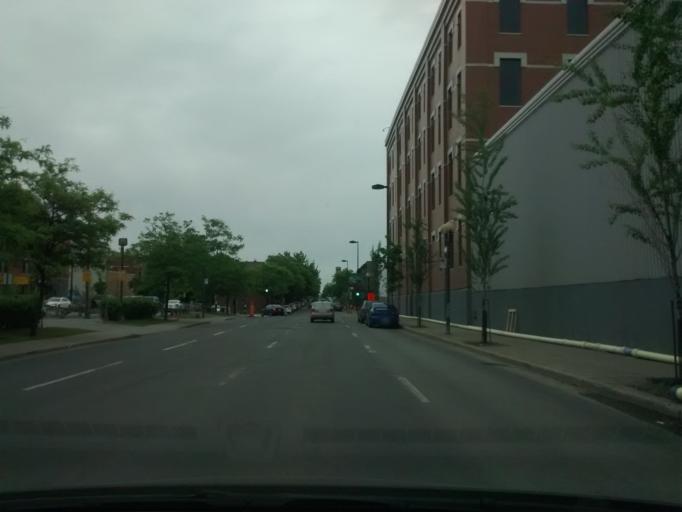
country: CA
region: Quebec
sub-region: Monteregie
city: Longueuil
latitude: 45.5329
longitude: -73.5543
